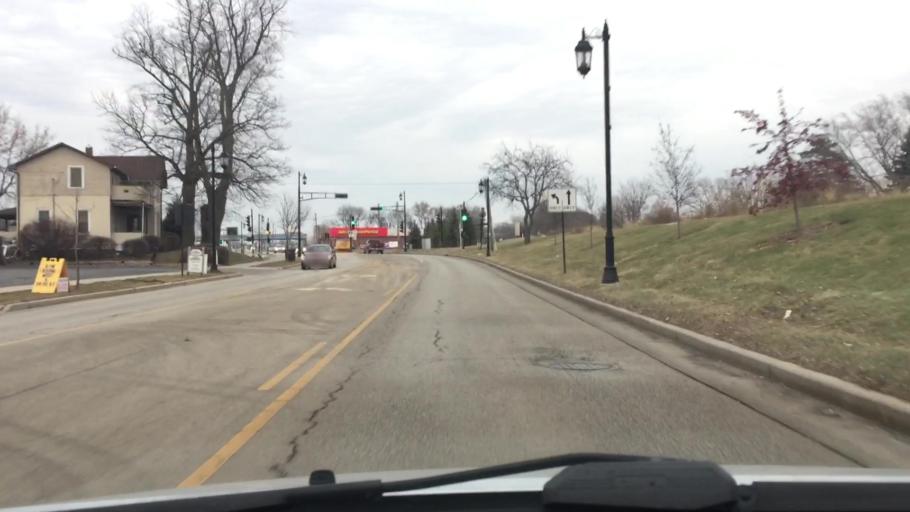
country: US
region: Wisconsin
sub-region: Waukesha County
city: Oconomowoc
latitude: 43.1071
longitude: -88.4872
